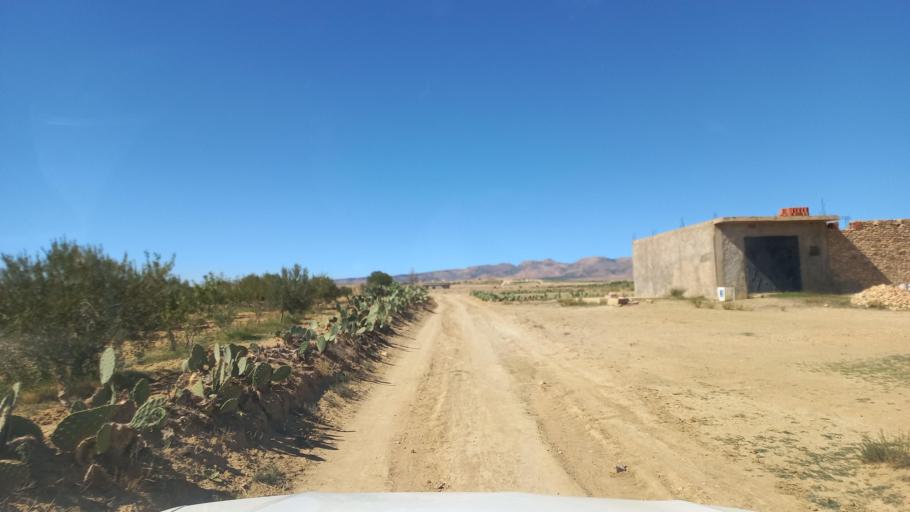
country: TN
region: Al Qasrayn
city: Sbiba
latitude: 35.3670
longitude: 9.0876
